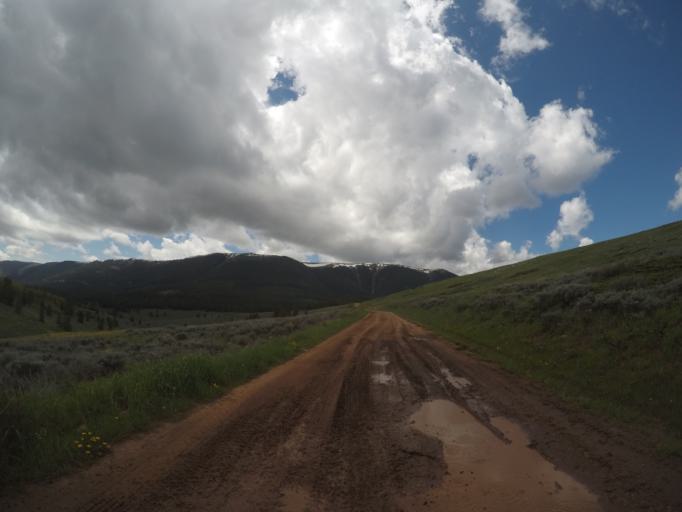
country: US
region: Wyoming
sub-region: Big Horn County
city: Lovell
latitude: 45.1802
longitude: -108.4399
